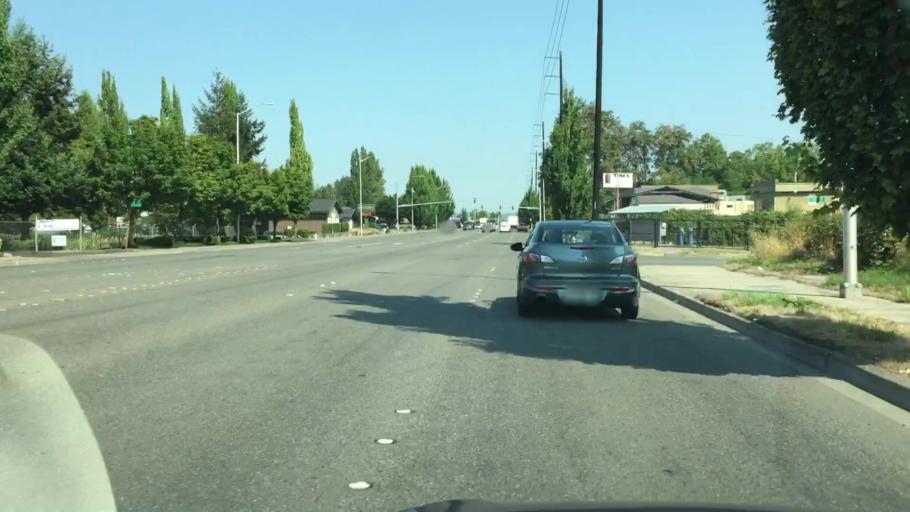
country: US
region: Washington
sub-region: King County
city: Kent
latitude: 47.4066
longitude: -122.2279
